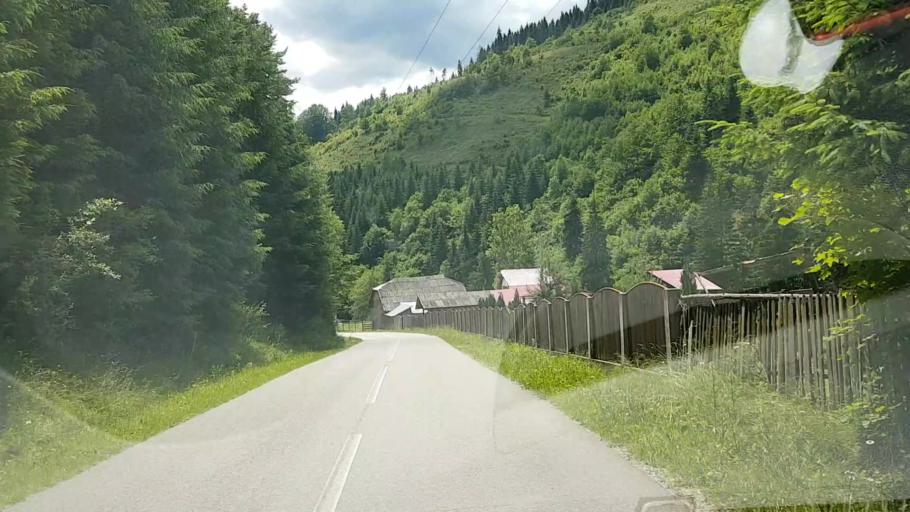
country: RO
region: Suceava
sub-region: Comuna Crucea
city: Crucea
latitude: 47.4222
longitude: 25.5792
